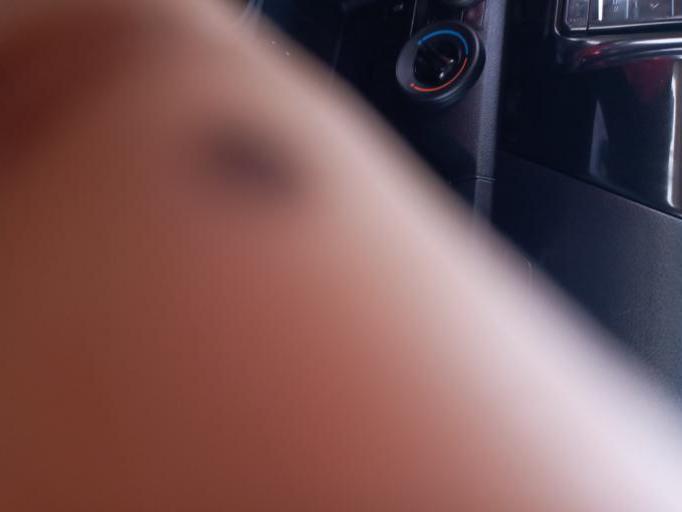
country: ET
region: Oromiya
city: Shashemene
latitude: 7.3046
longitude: 38.6186
